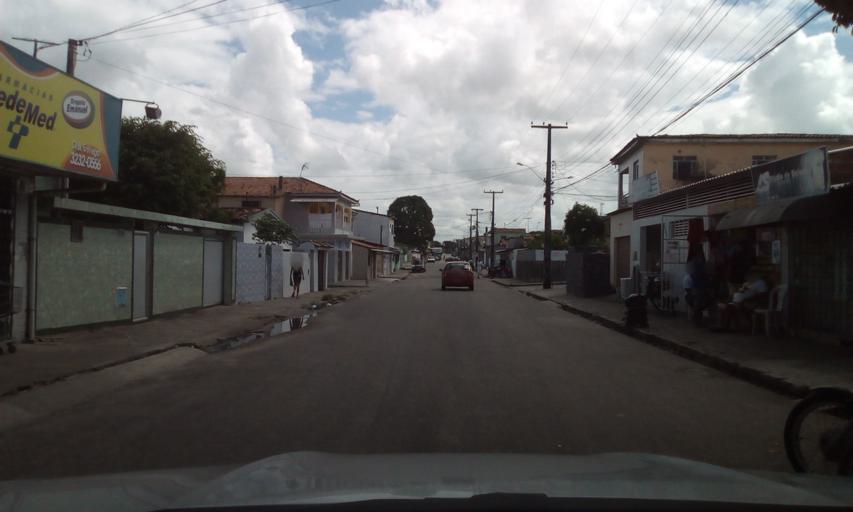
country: BR
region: Paraiba
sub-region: Bayeux
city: Bayeux
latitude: -7.1359
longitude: -34.9219
